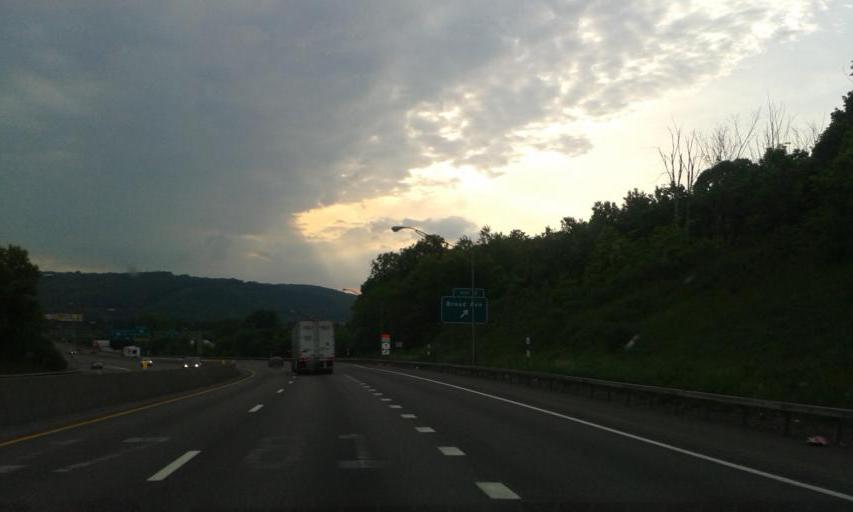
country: US
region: New York
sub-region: Broome County
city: Port Dickinson
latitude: 42.1148
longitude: -75.8830
